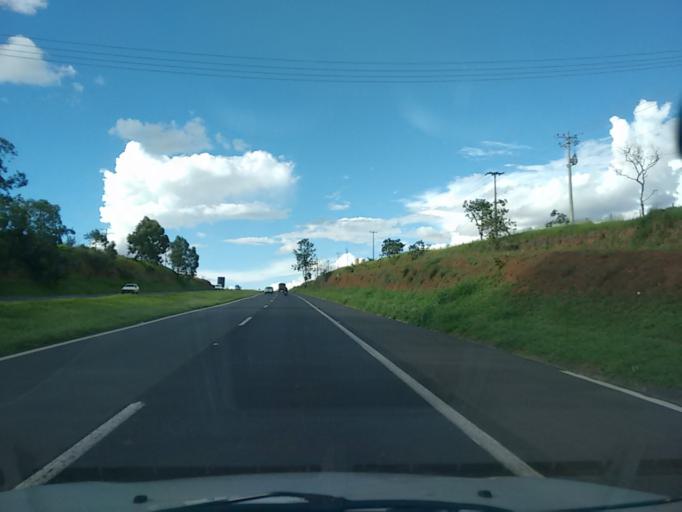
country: BR
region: Sao Paulo
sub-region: Sao Carlos
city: Sao Carlos
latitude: -22.0312
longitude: -47.8598
